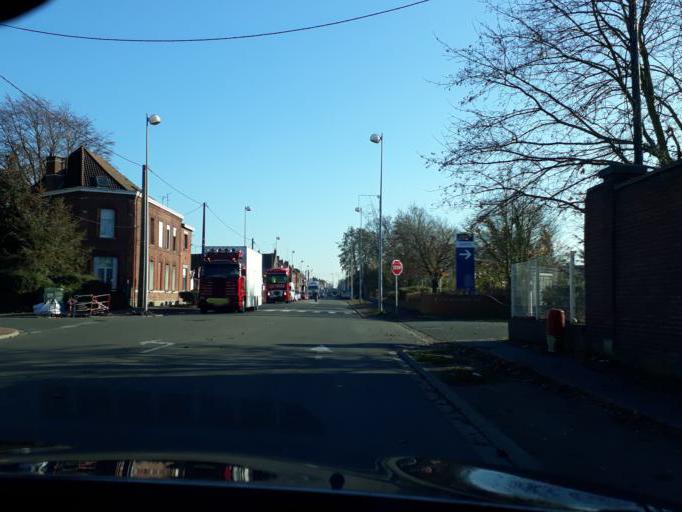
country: FR
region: Nord-Pas-de-Calais
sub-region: Departement du Nord
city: Auberchicourt
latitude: 50.3319
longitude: 3.2397
